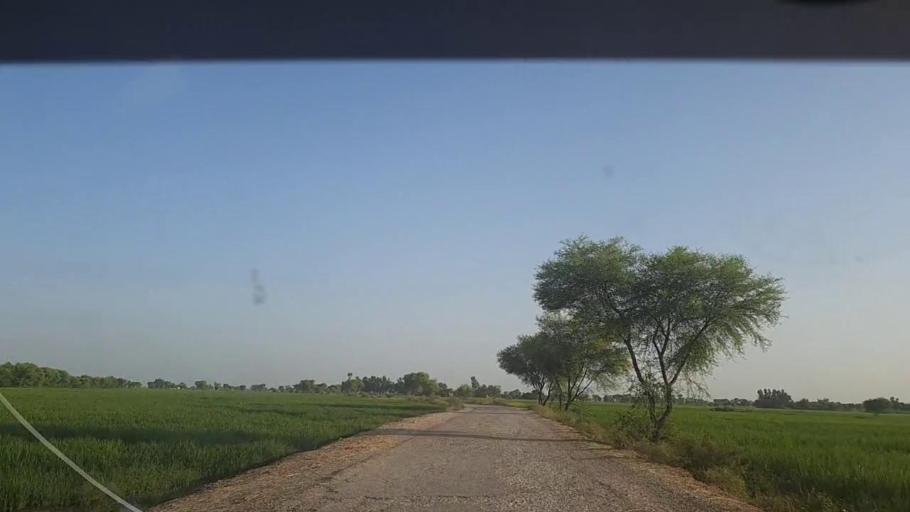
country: PK
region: Sindh
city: Thul
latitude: 28.2099
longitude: 68.8703
